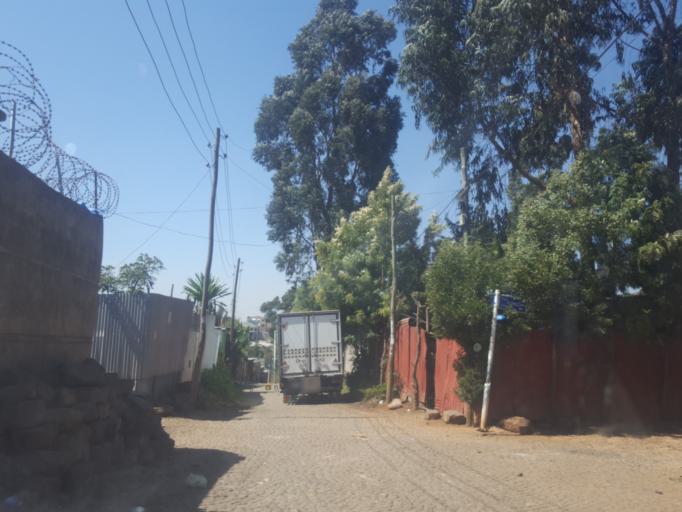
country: ET
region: Adis Abeba
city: Addis Ababa
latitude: 9.0589
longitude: 38.7231
